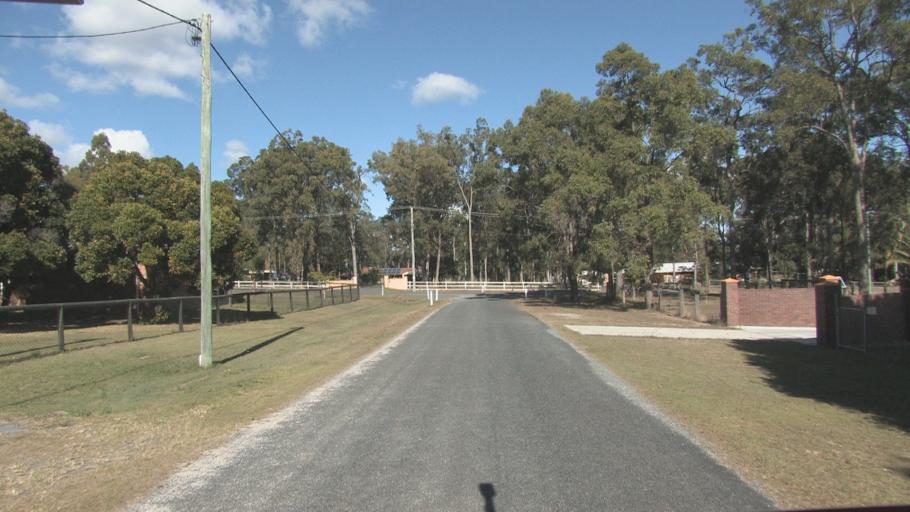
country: AU
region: Queensland
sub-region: Logan
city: Chambers Flat
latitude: -27.7465
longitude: 153.0975
